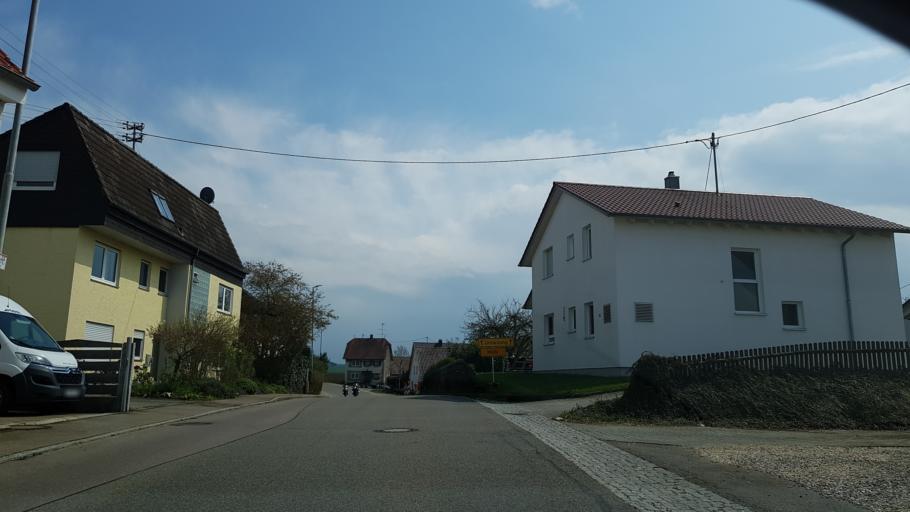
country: DE
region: Baden-Wuerttemberg
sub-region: Tuebingen Region
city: Wain
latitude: 48.2091
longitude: 10.0206
